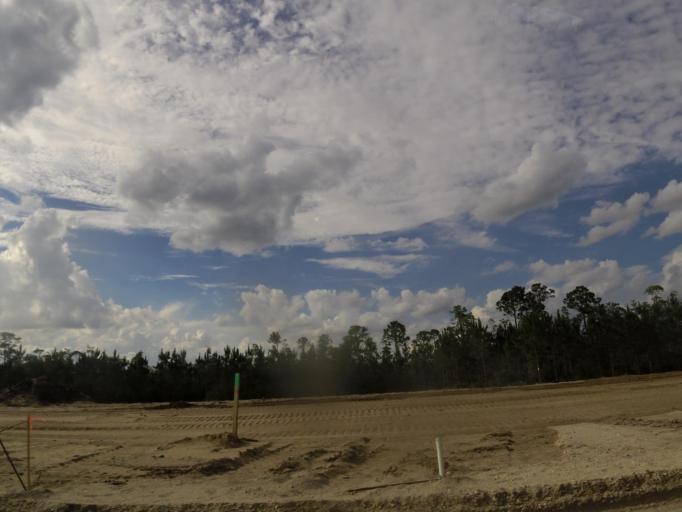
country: US
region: Florida
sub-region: Saint Johns County
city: Palm Valley
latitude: 30.1823
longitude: -81.5080
